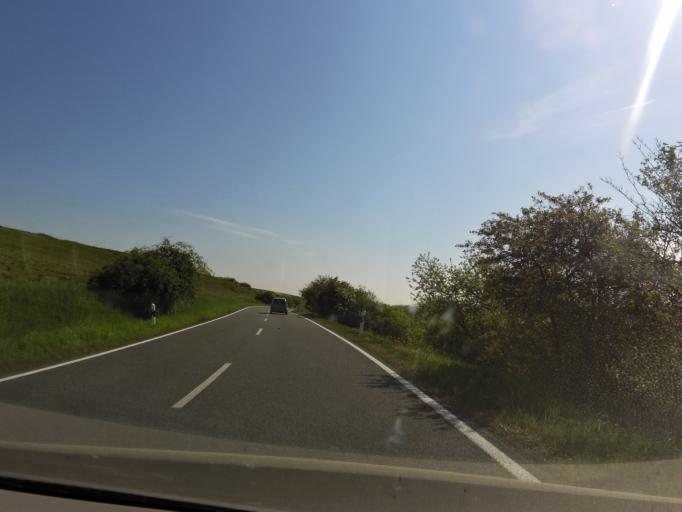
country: DE
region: Thuringia
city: Walschleben
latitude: 51.0415
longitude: 10.9154
